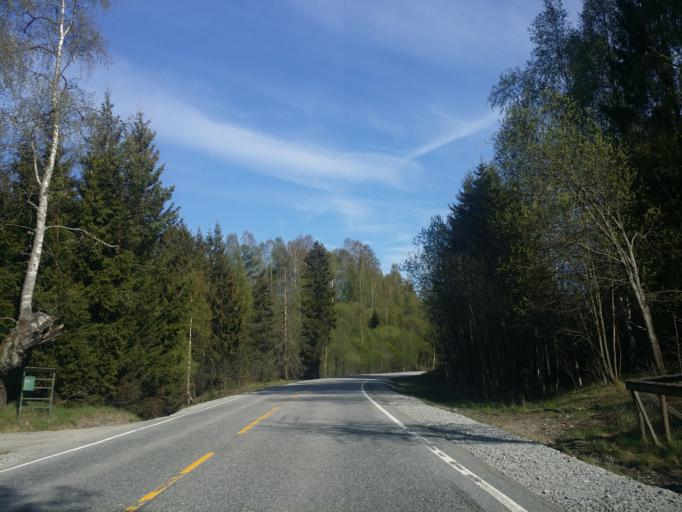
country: NO
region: Telemark
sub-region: Hjartdal
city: Sauland
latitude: 59.6230
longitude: 8.9081
